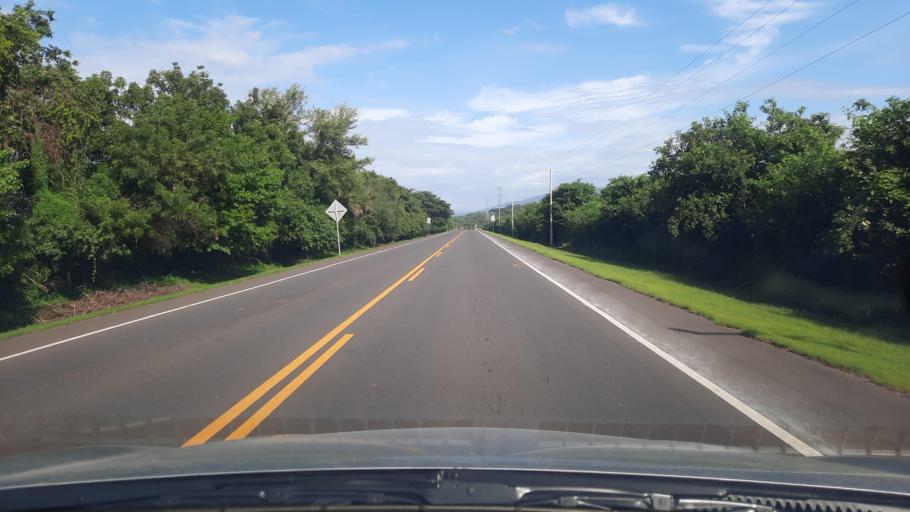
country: NI
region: Chinandega
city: Chichigalpa
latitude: 12.7436
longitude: -86.8925
